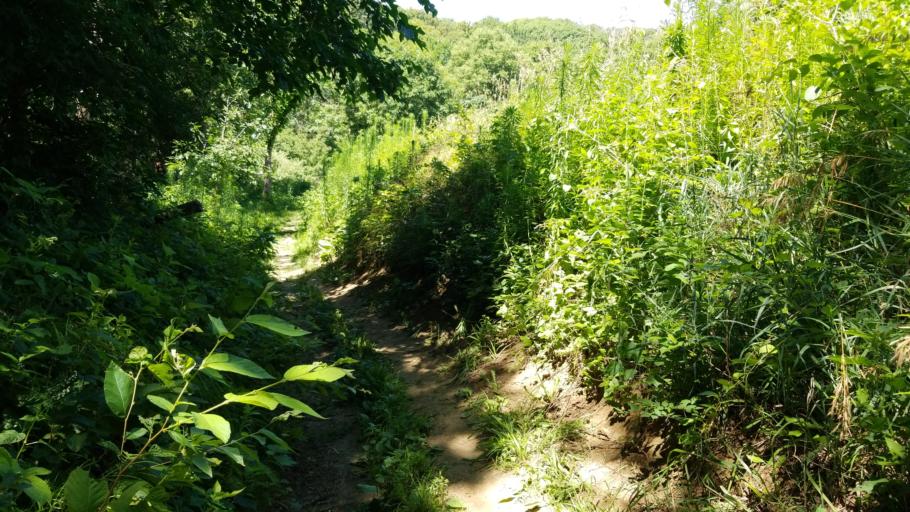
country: US
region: Iowa
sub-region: Pottawattamie County
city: Carter Lake
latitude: 41.3912
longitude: -95.9528
